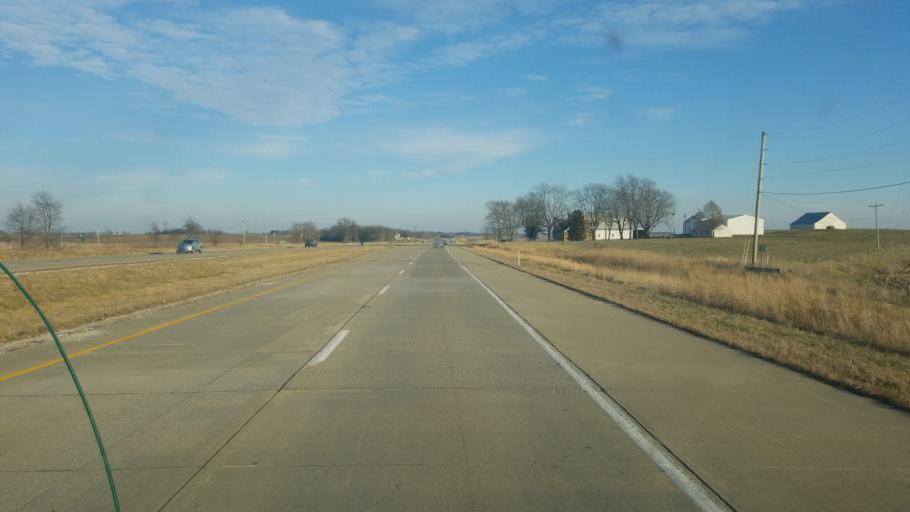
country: US
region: Indiana
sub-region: Knox County
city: Bicknell
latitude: 38.6733
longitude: -87.3603
